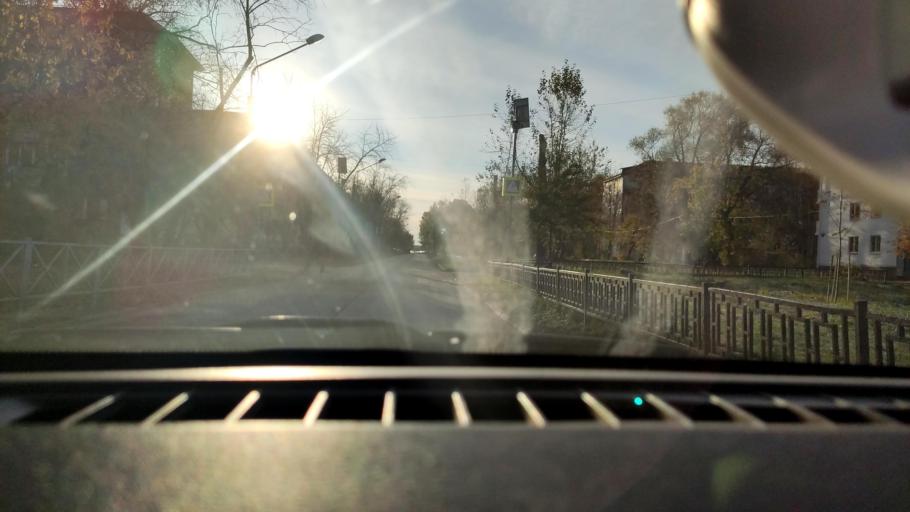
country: RU
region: Perm
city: Perm
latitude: 57.9966
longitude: 56.2955
